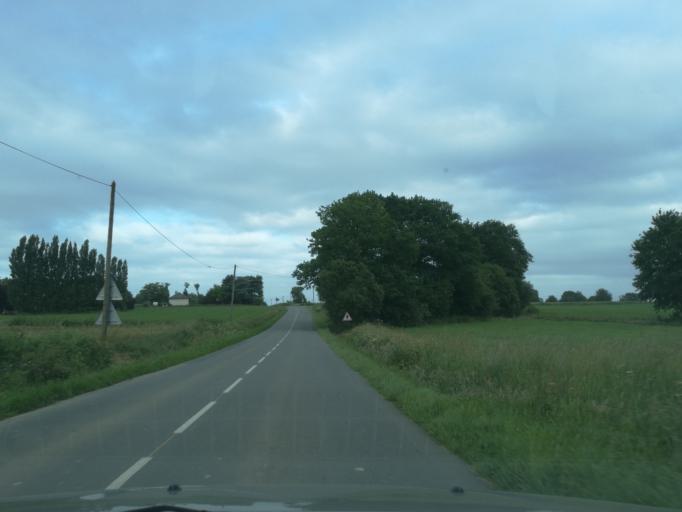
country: FR
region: Brittany
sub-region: Departement d'Ille-et-Vilaine
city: Bedee
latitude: 48.2056
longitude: -1.9673
